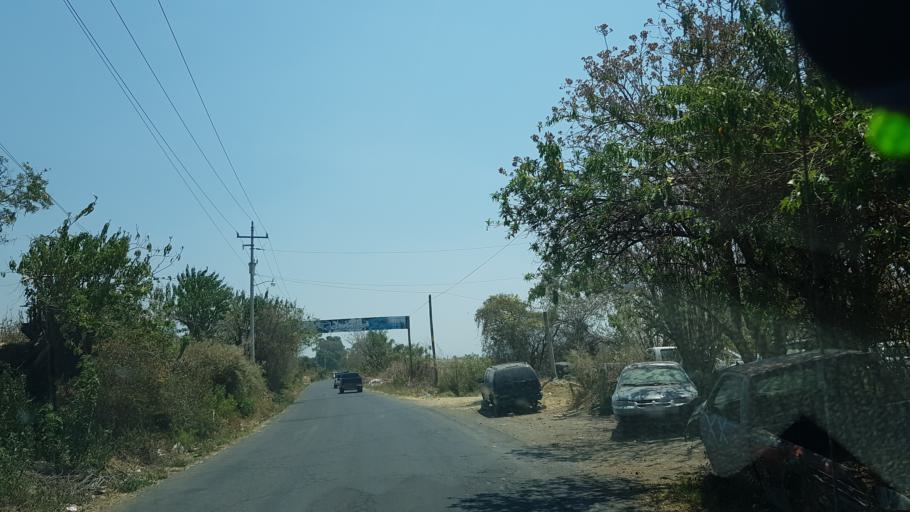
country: MX
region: Puebla
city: Tochimilco
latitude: 18.8865
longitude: -98.5523
